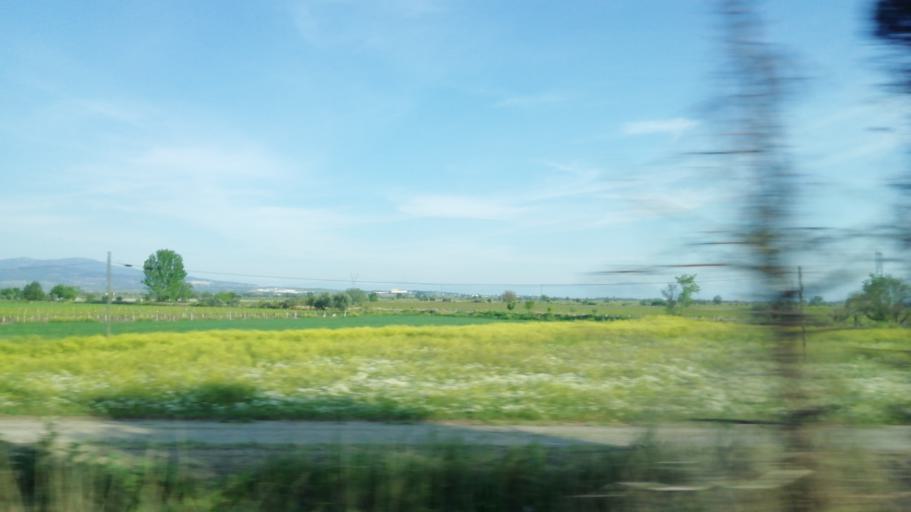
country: TR
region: Manisa
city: Saruhanli
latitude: 38.7202
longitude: 27.5607
